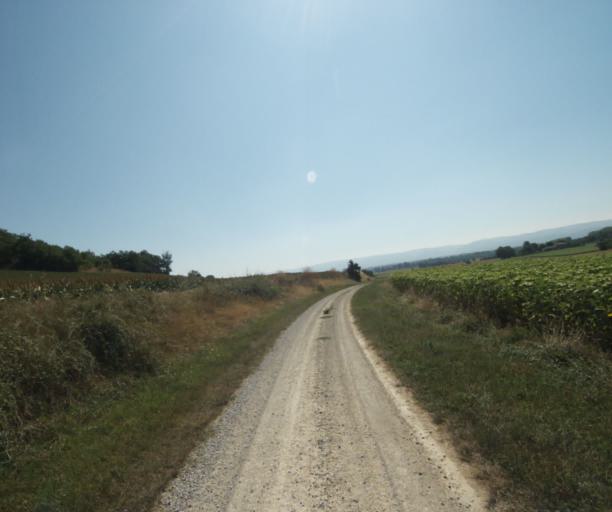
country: FR
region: Midi-Pyrenees
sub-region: Departement de la Haute-Garonne
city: Revel
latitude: 43.5107
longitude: 1.9441
